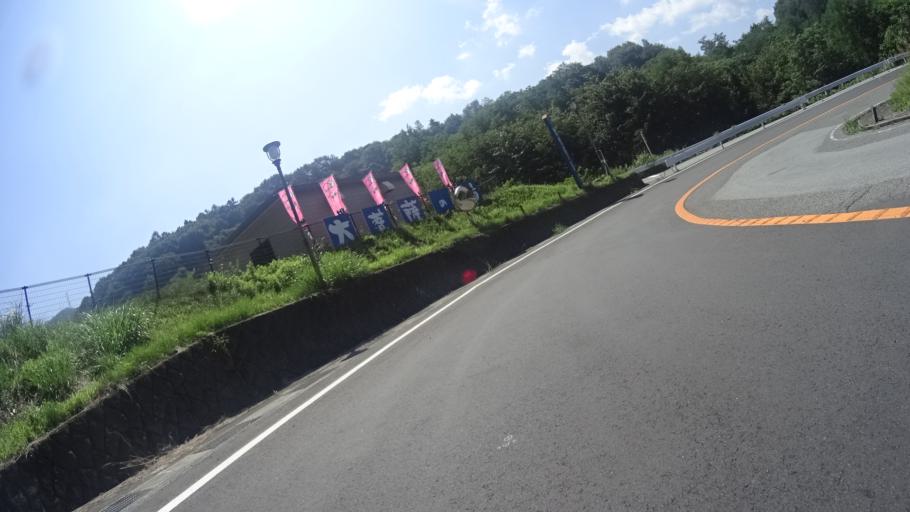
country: JP
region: Yamanashi
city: Enzan
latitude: 35.7343
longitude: 138.7959
